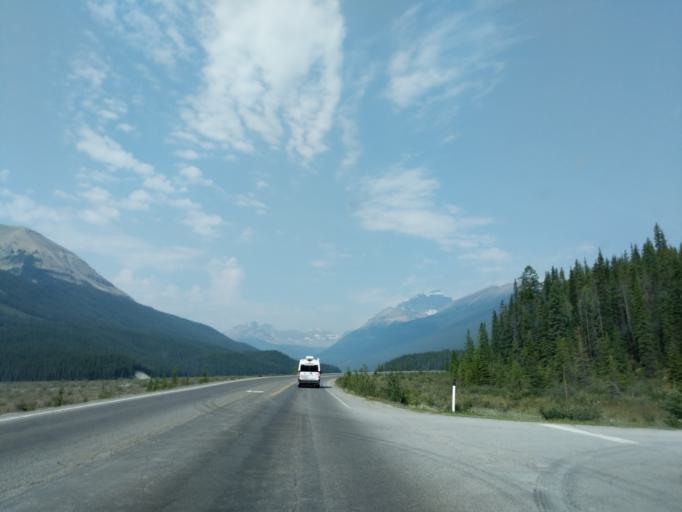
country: CA
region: British Columbia
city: Golden
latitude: 52.0684
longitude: -116.9098
